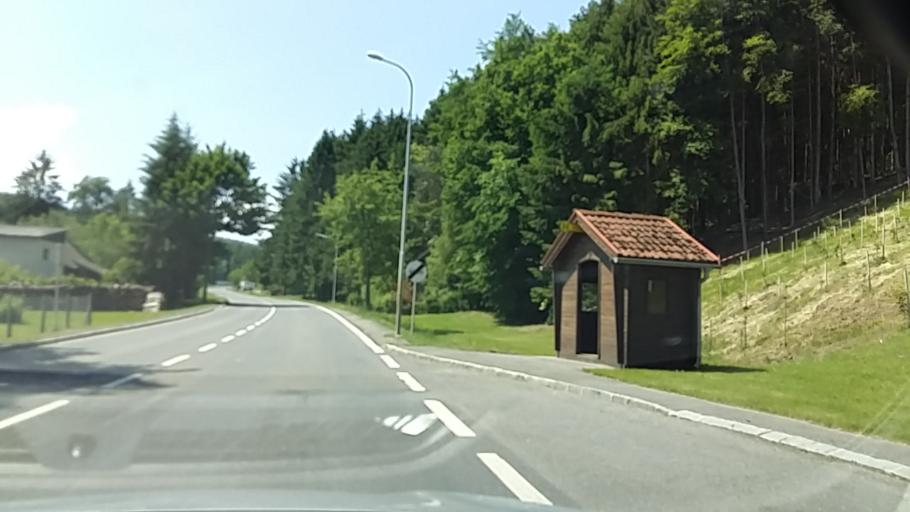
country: AT
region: Burgenland
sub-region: Politischer Bezirk Oberpullendorf
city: Lockenhaus
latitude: 47.4028
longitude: 16.3734
